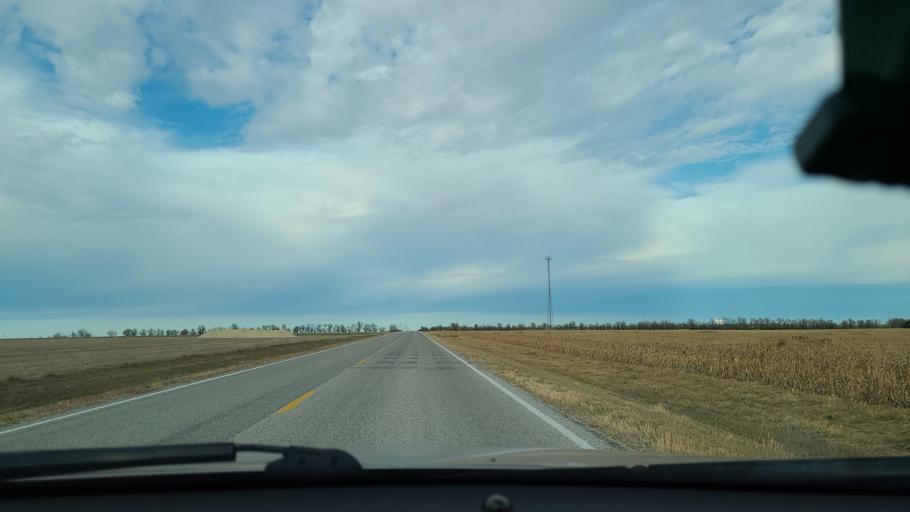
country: US
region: Kansas
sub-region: McPherson County
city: Inman
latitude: 38.3567
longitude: -97.9244
